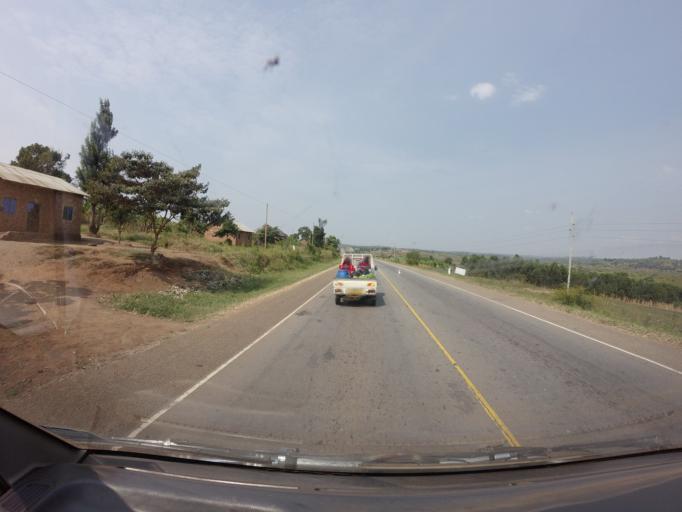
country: UG
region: Central Region
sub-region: Lwengo District
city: Lwengo
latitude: -0.4046
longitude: 31.3677
